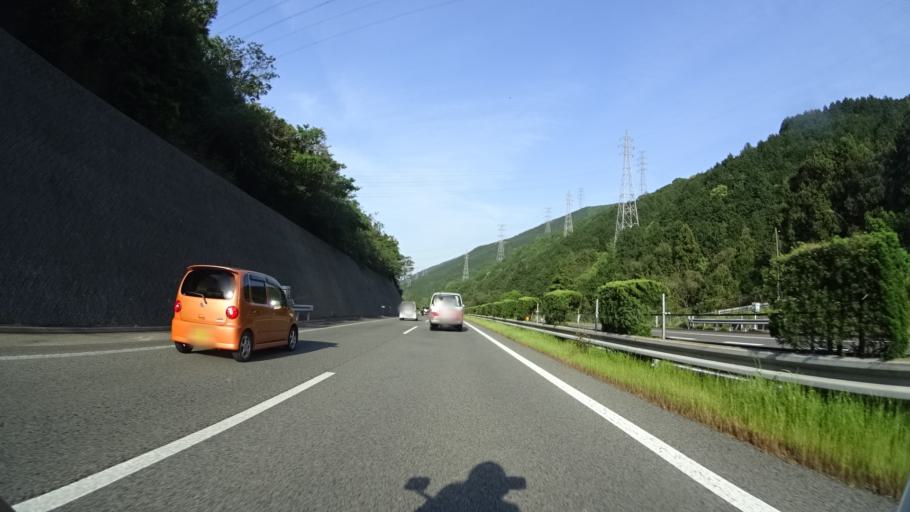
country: JP
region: Ehime
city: Niihama
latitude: 33.9416
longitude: 133.3944
